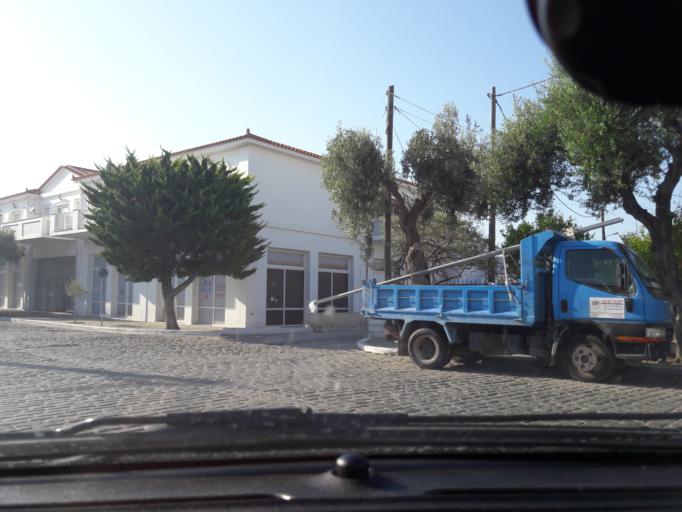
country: GR
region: North Aegean
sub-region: Nomos Lesvou
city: Myrina
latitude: 39.8728
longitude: 25.0629
